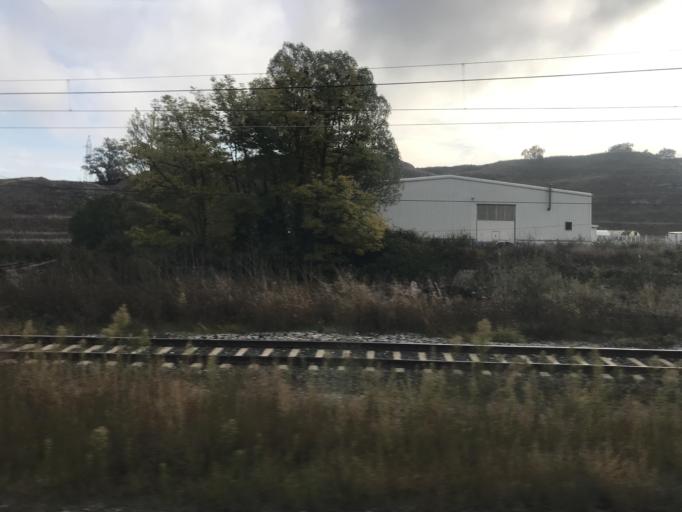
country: ES
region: Castille and Leon
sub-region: Provincia de Burgos
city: Briviesca
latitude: 42.5403
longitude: -3.3190
